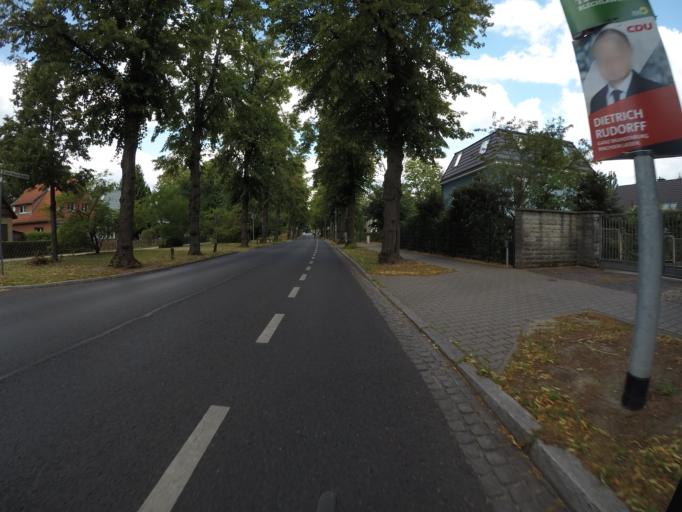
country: DE
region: Brandenburg
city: Kleinmachnow
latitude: 52.4179
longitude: 13.2260
